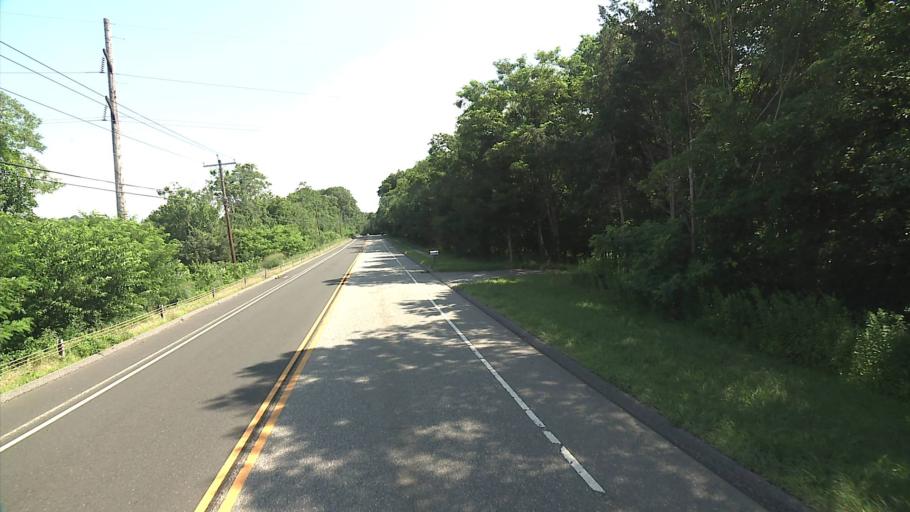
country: US
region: Connecticut
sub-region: Middlesex County
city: Westbrook Center
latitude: 41.3193
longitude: -72.4319
